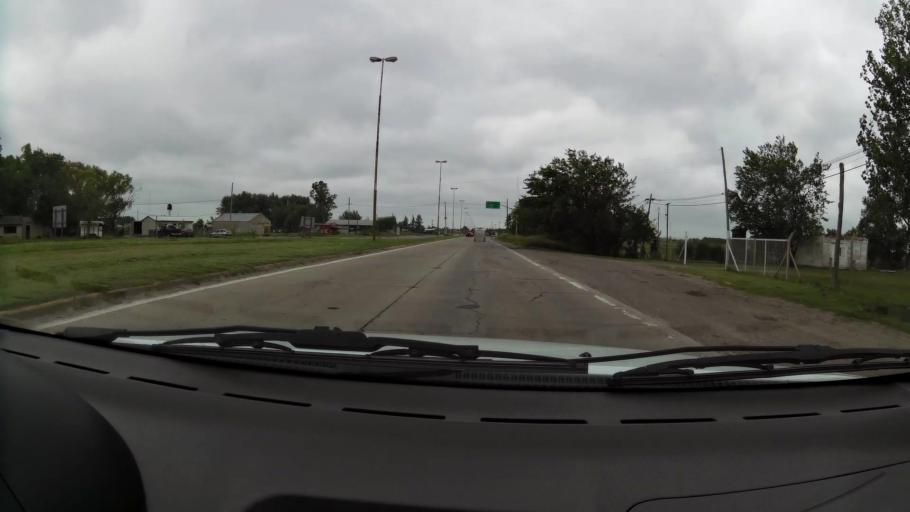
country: AR
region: Buenos Aires
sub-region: Partido de Brandsen
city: Brandsen
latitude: -35.0504
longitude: -58.1085
